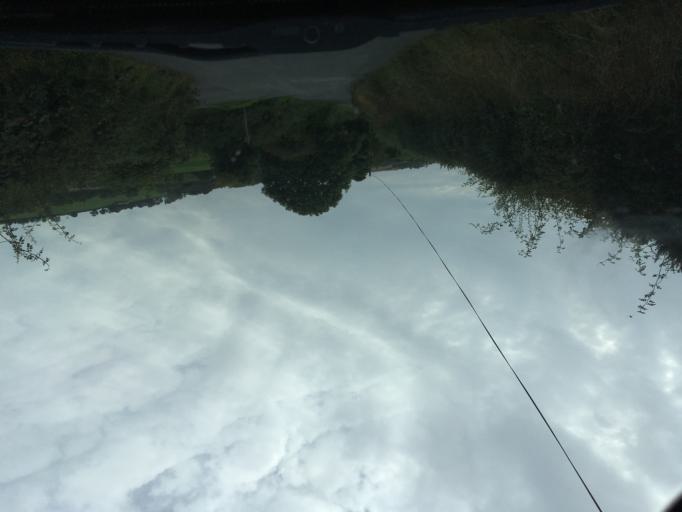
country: IE
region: Leinster
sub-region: Wicklow
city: Rathnew
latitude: 52.9232
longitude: -6.1077
